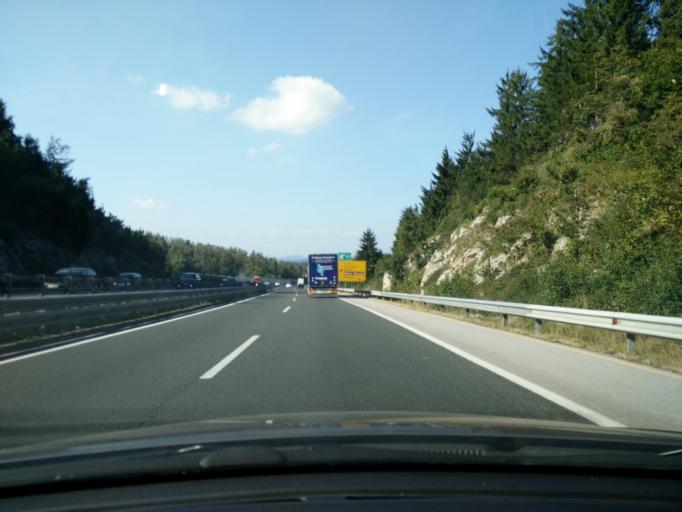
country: SI
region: Cerknica
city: Rakek
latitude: 45.8150
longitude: 14.2862
